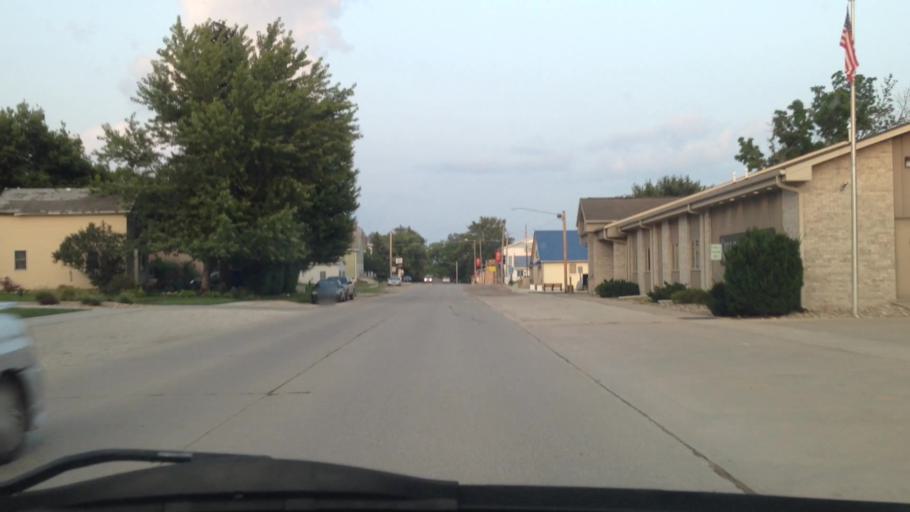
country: US
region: Iowa
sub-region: Linn County
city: Palo
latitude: 42.0945
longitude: -91.8719
